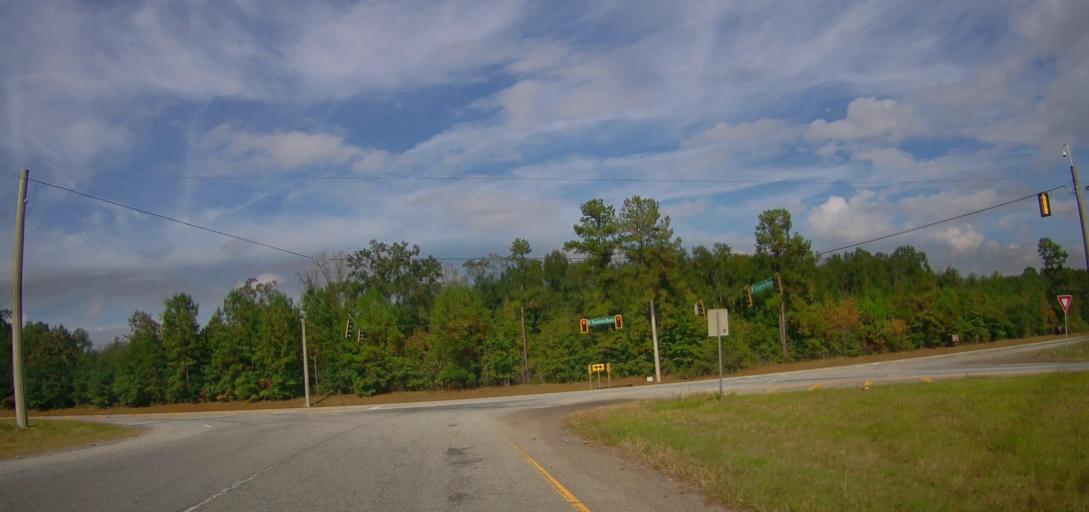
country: US
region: Georgia
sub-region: Thomas County
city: Thomasville
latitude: 30.8683
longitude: -84.0066
